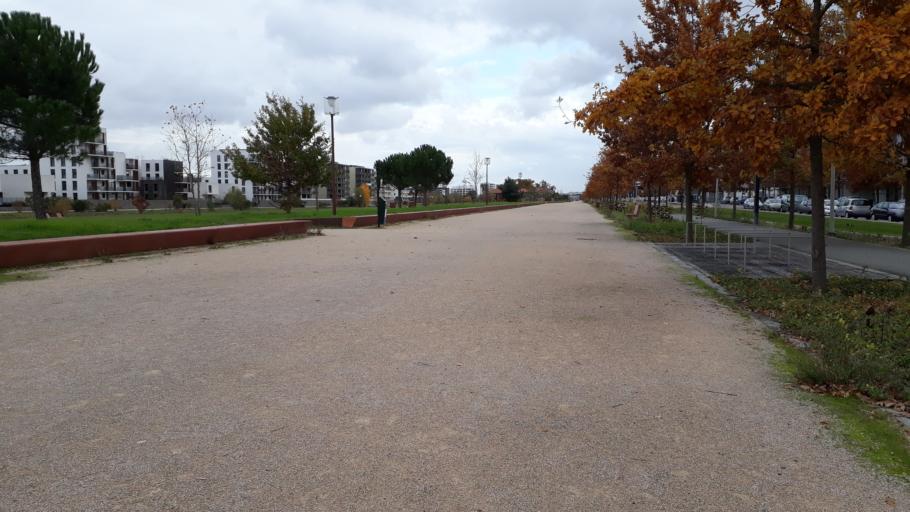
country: FR
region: Midi-Pyrenees
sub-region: Departement de la Haute-Garonne
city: Beauzelle
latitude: 43.6614
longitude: 1.3689
